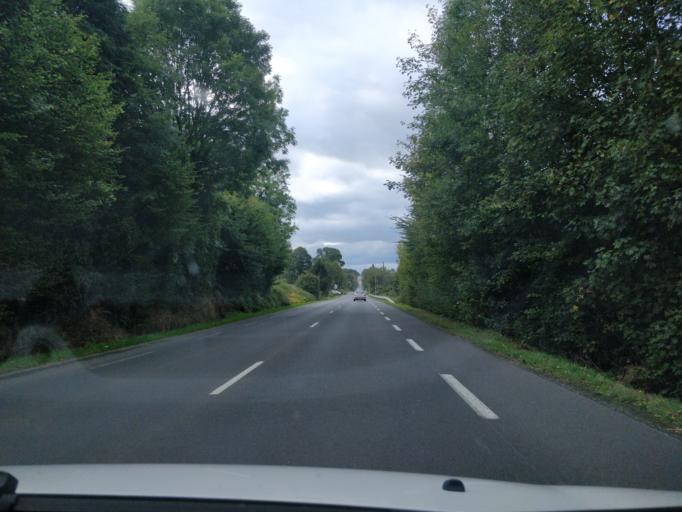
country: FR
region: Lower Normandy
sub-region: Departement du Calvados
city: Vire
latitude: 48.8428
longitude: -0.9304
